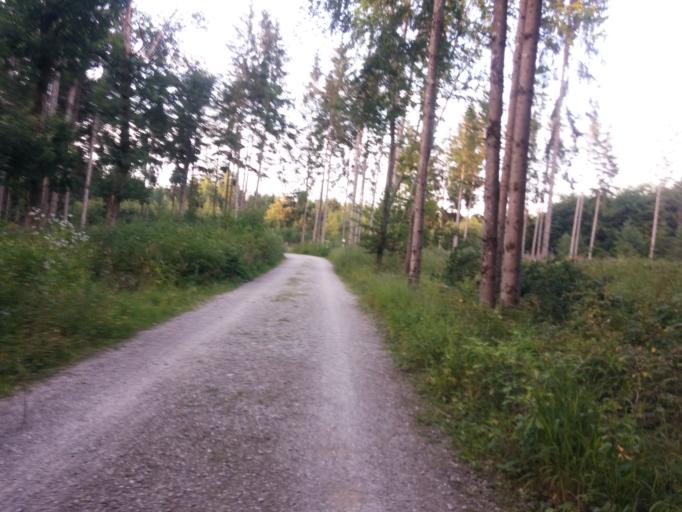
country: DE
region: Bavaria
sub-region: Upper Bavaria
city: Grasbrunn
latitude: 48.0651
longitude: 11.7614
